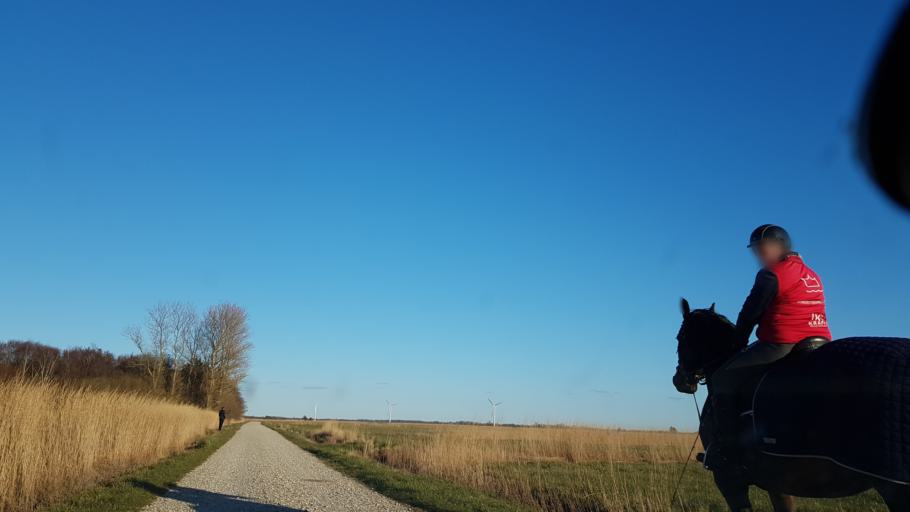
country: DK
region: South Denmark
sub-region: Esbjerg Kommune
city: Bramming
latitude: 55.4152
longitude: 8.6530
